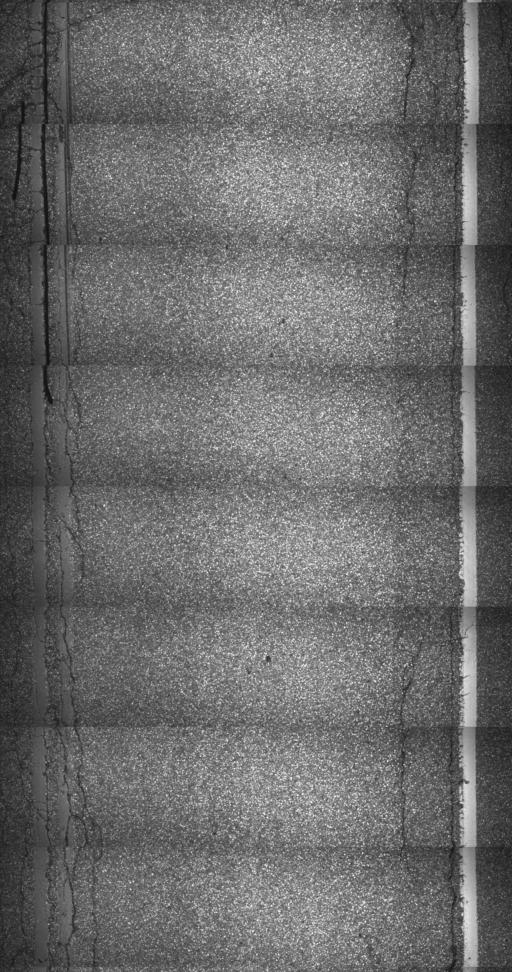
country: US
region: Vermont
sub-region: Windsor County
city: Chester
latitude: 43.3675
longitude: -72.7918
